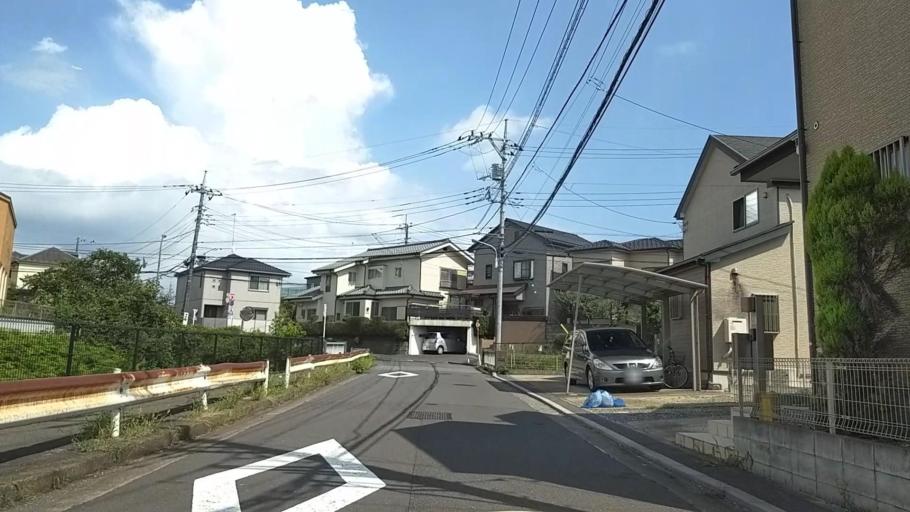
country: JP
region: Tokyo
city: Hachioji
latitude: 35.6454
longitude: 139.3162
